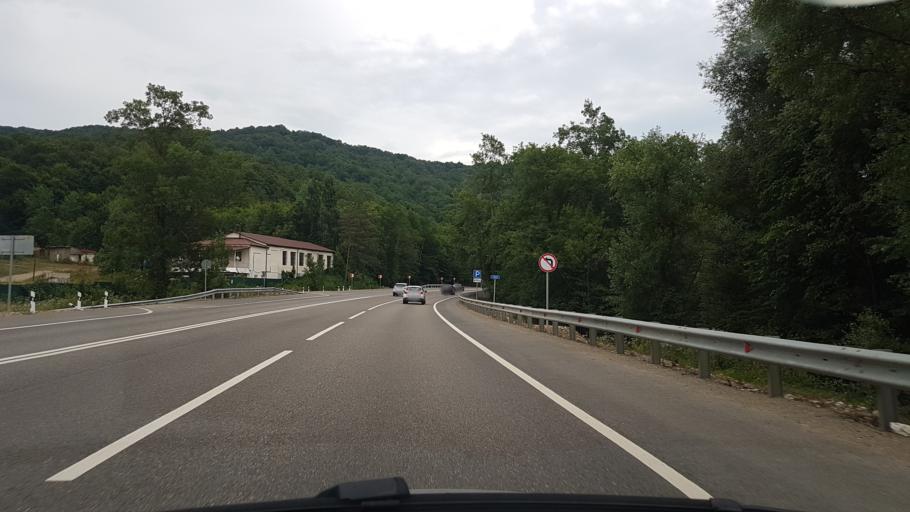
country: RU
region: Krasnodarskiy
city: Dzhubga
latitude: 44.4014
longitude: 38.7374
